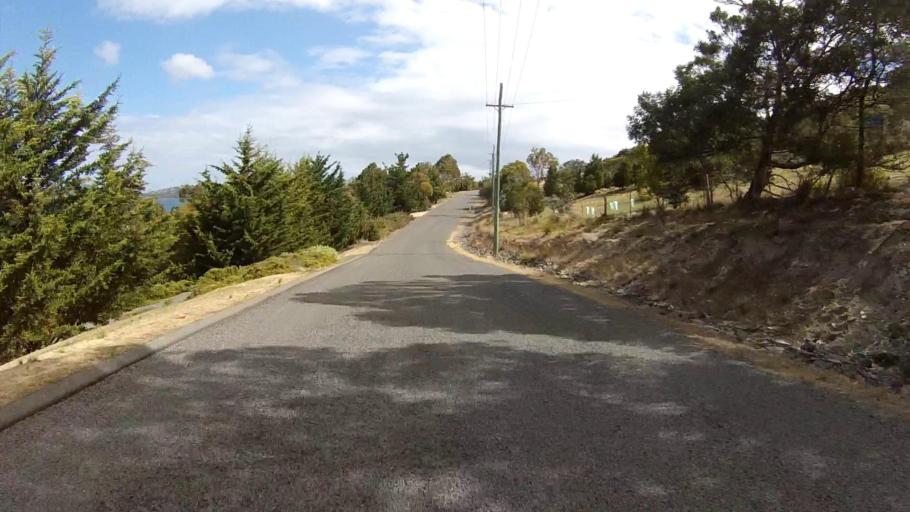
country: AU
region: Tasmania
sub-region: Clarence
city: Acton Park
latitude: -42.8821
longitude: 147.5039
